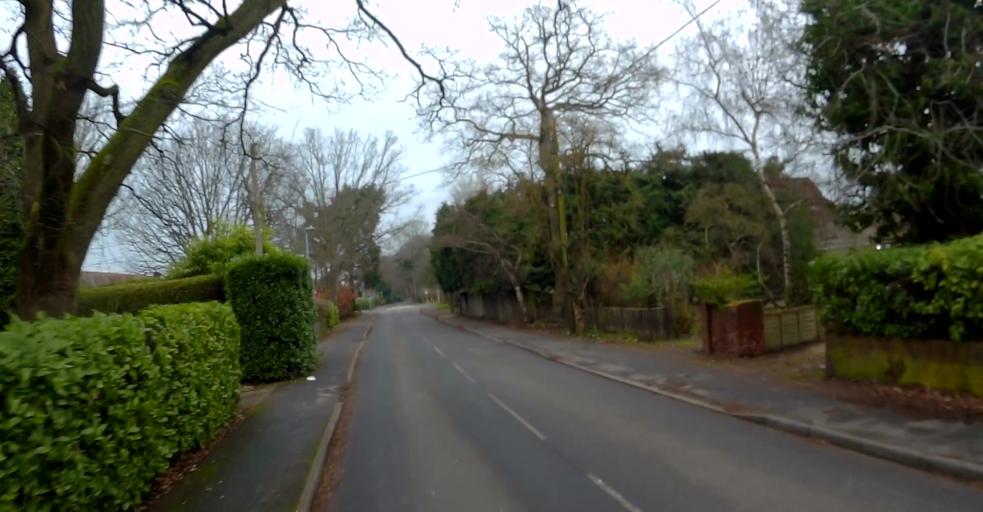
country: GB
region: England
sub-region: Wokingham
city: Barkham
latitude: 51.3847
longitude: -0.8581
